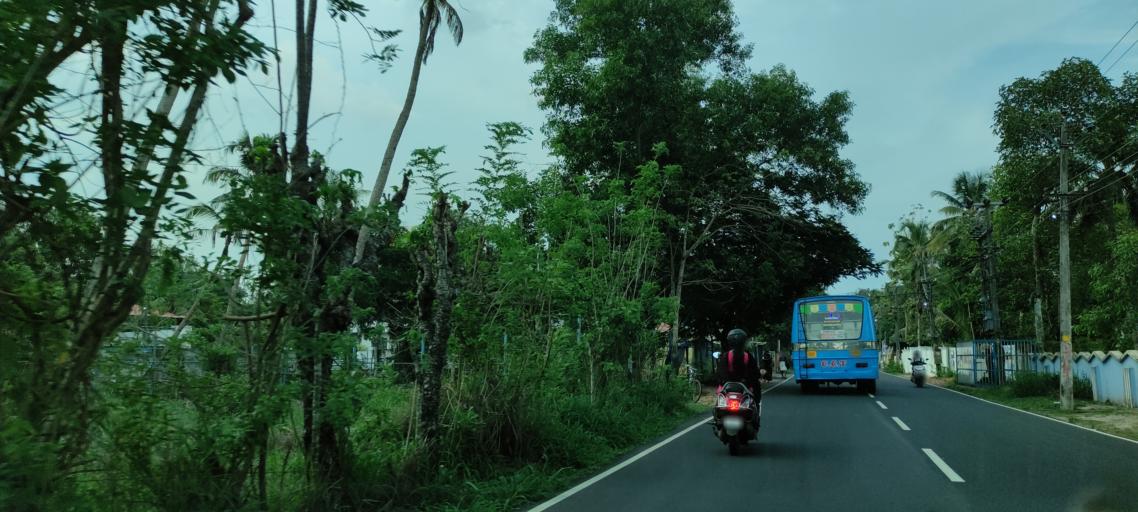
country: IN
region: Kerala
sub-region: Alappuzha
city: Kutiatodu
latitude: 9.7875
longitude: 76.3593
